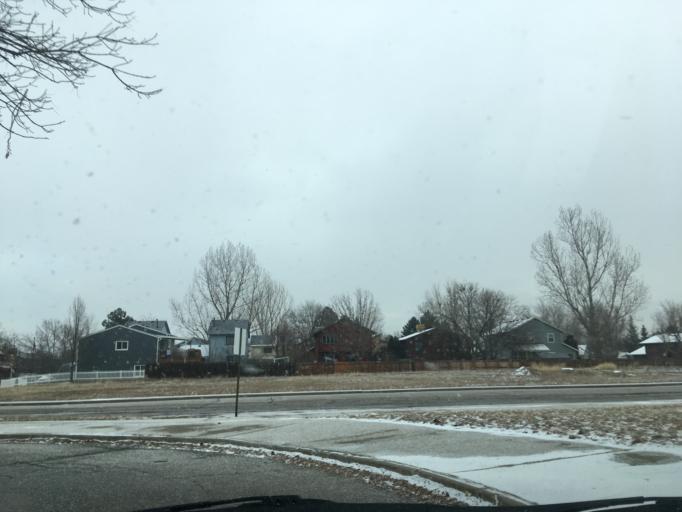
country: US
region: Colorado
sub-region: Boulder County
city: Lafayette
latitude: 39.9898
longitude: -105.0836
